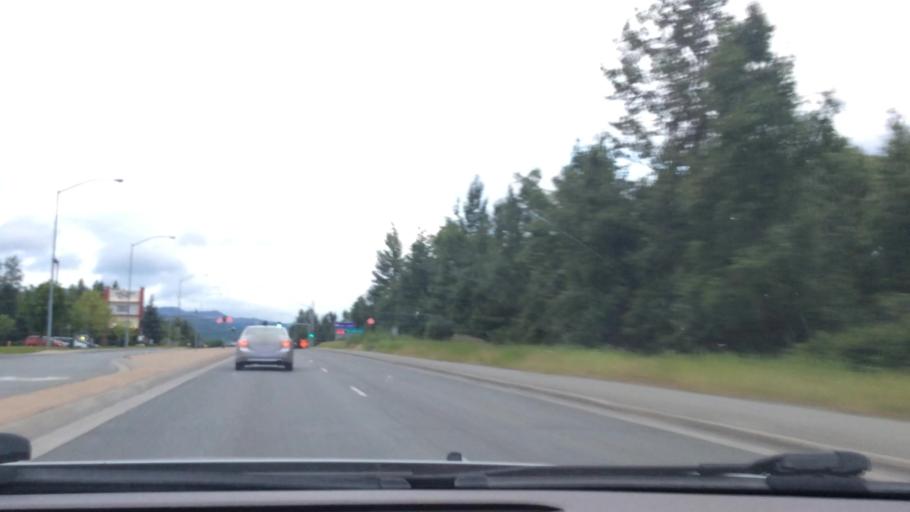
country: US
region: Alaska
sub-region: Anchorage Municipality
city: Elmendorf Air Force Base
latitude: 61.1939
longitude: -149.7336
